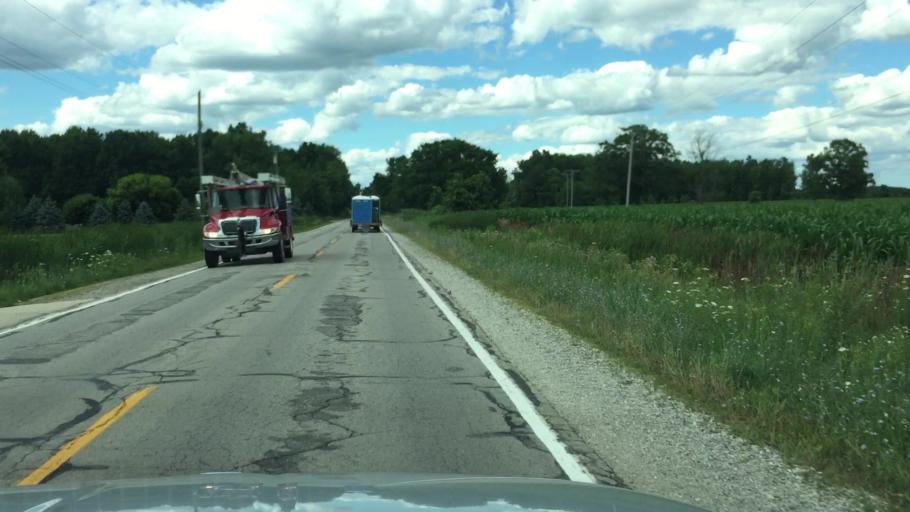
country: US
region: Michigan
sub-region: Saint Clair County
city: Capac
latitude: 42.9364
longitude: -82.9458
